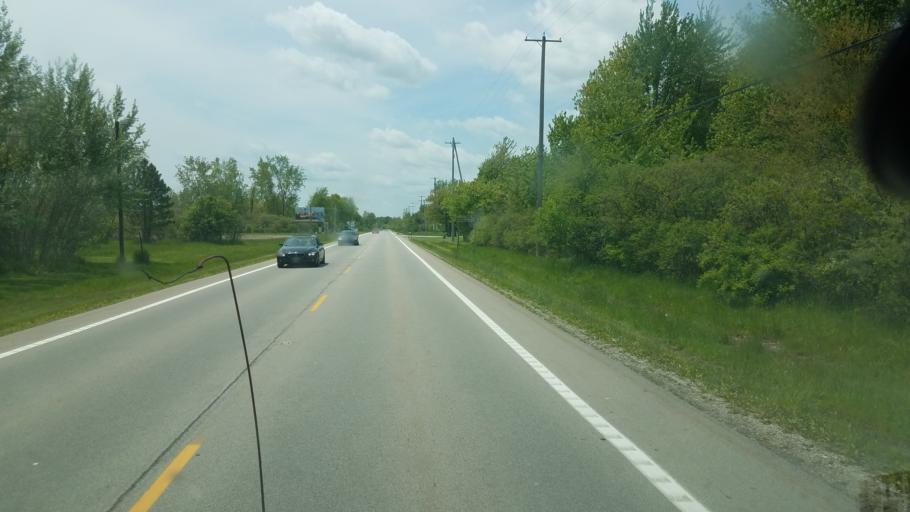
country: US
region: Ohio
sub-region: Ottawa County
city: Port Clinton
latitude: 41.4719
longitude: -83.0329
